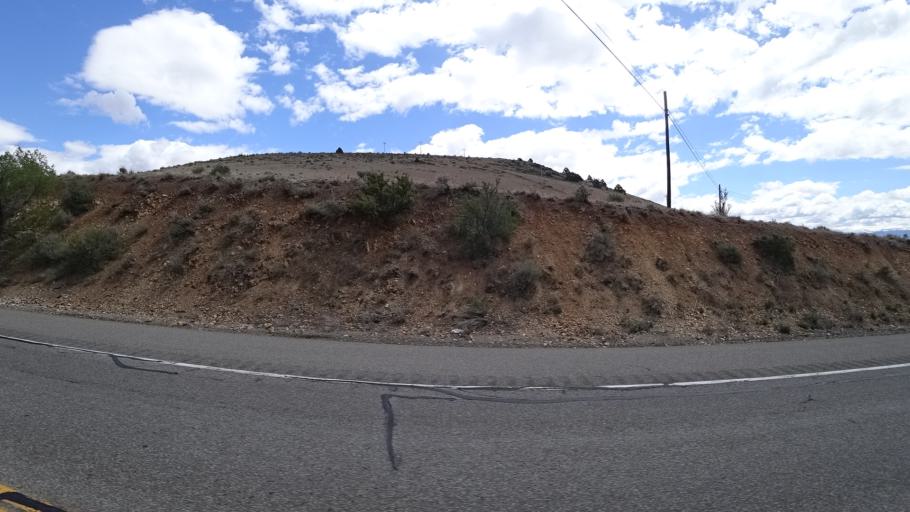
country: US
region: Nevada
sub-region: Lyon County
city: Smith Valley
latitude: 38.7108
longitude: -119.5533
